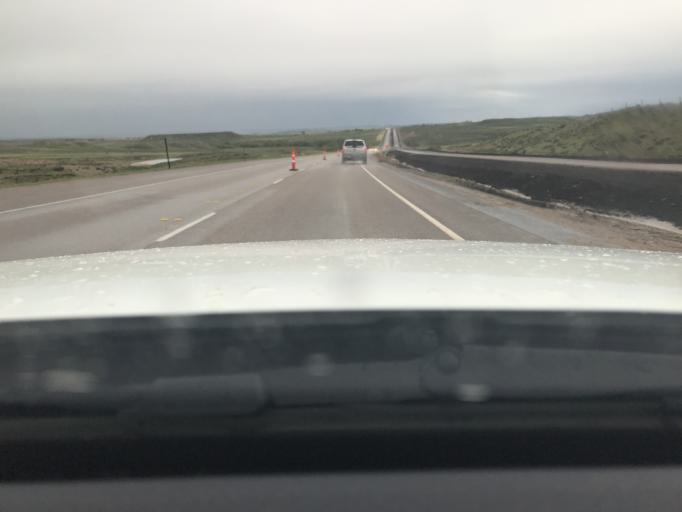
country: US
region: Wyoming
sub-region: Converse County
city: Douglas
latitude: 42.7924
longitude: -105.5526
